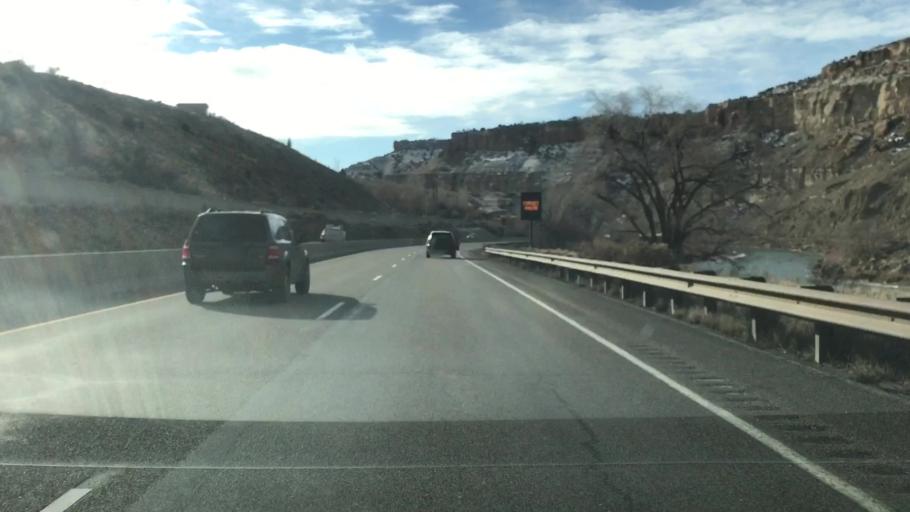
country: US
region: Colorado
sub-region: Mesa County
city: Palisade
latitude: 39.1338
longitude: -108.3225
